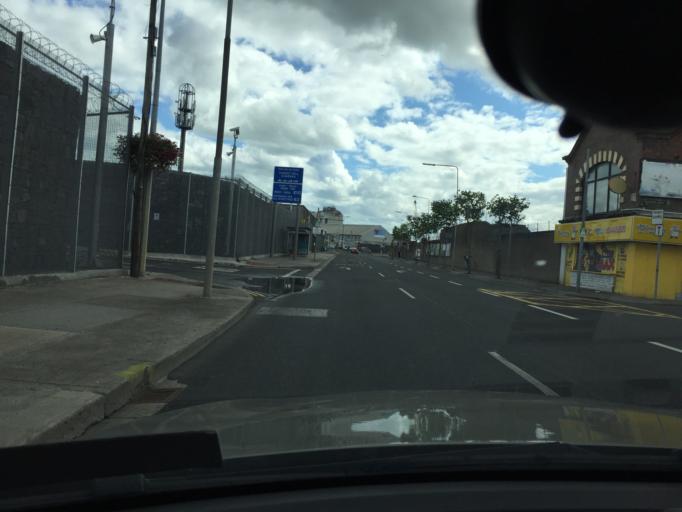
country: IE
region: Leinster
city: Ringsend
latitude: 53.3538
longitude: -6.2272
